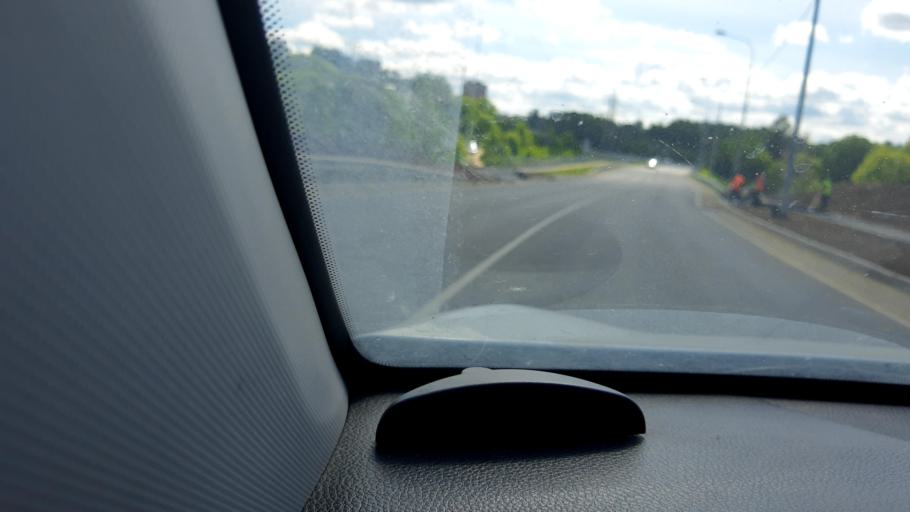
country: RU
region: Moskovskaya
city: Vidnoye
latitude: 55.5373
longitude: 37.7011
